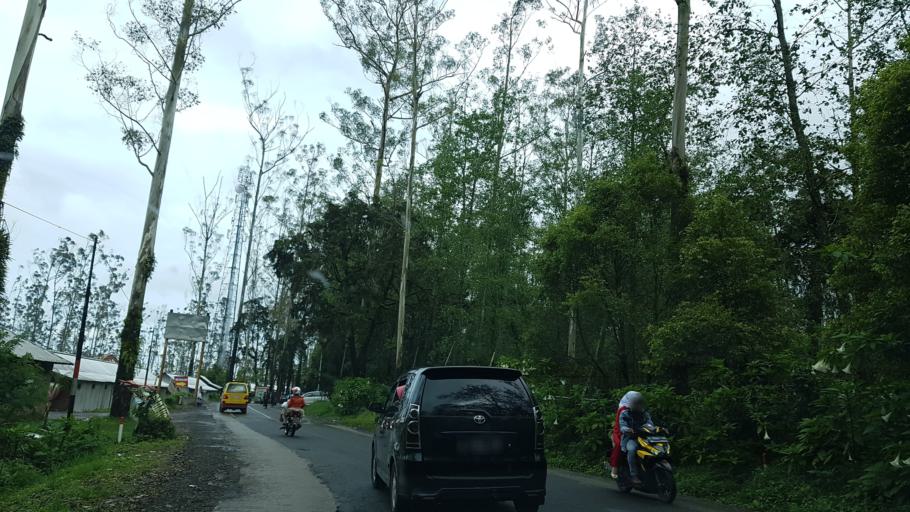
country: ID
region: West Java
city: Banjar
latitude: -7.1414
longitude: 107.3965
